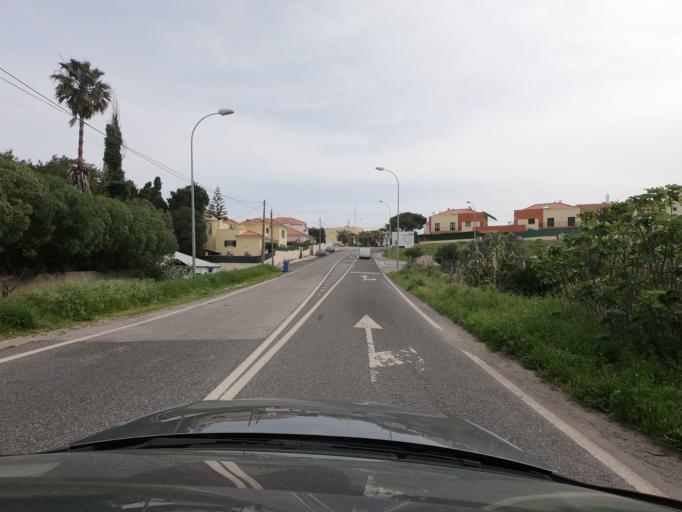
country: PT
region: Lisbon
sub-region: Oeiras
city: Barcarena
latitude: 38.7278
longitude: -9.2865
